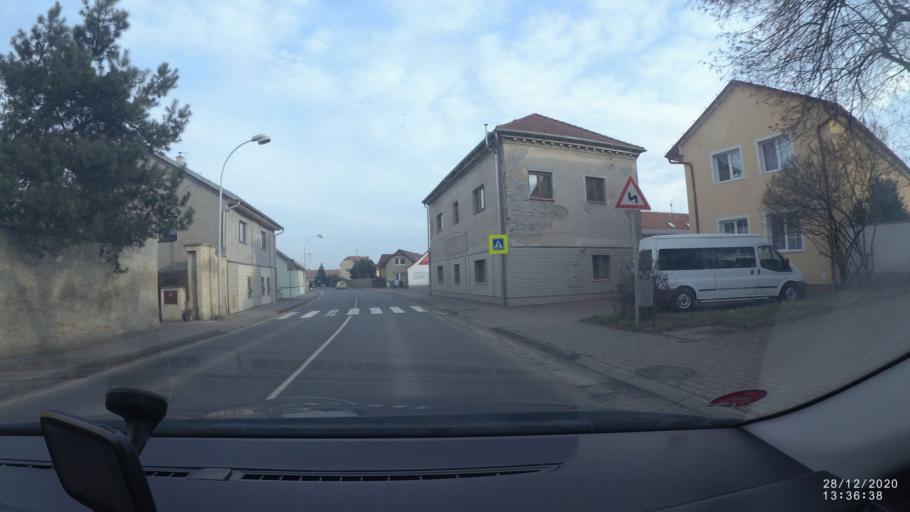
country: CZ
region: Central Bohemia
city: Nehvizdy
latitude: 50.1309
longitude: 14.7318
